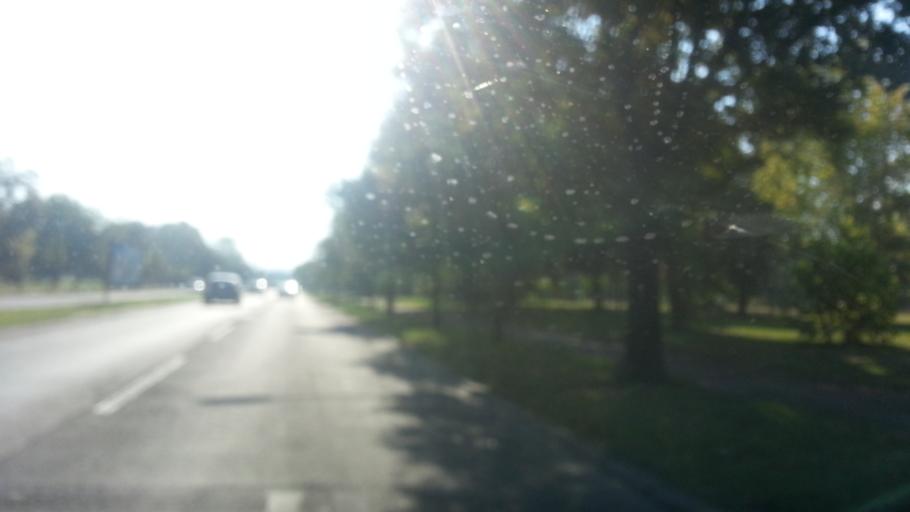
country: RS
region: Central Serbia
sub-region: Belgrade
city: Novi Beograd
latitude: 44.8204
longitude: 20.4312
